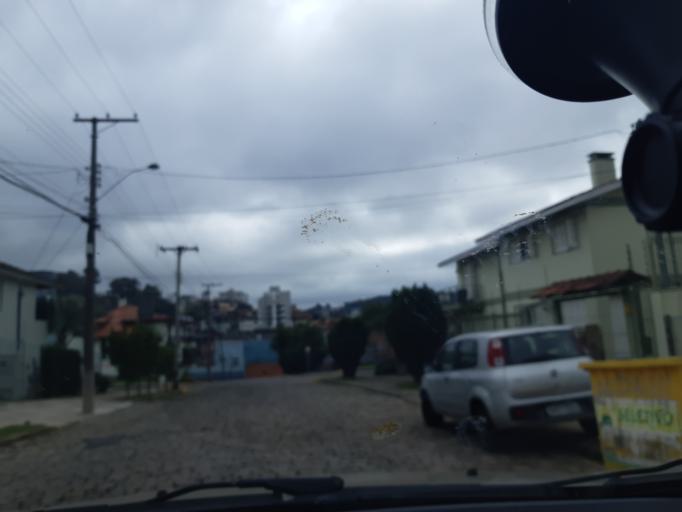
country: BR
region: Rio Grande do Sul
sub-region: Caxias Do Sul
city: Caxias do Sul
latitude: -29.1557
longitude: -51.2066
